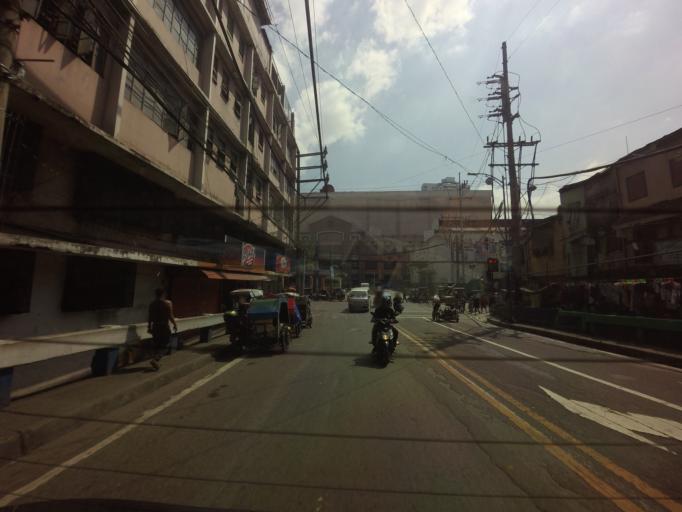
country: PH
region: Metro Manila
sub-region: City of Manila
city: Manila
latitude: 14.6093
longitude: 120.9718
